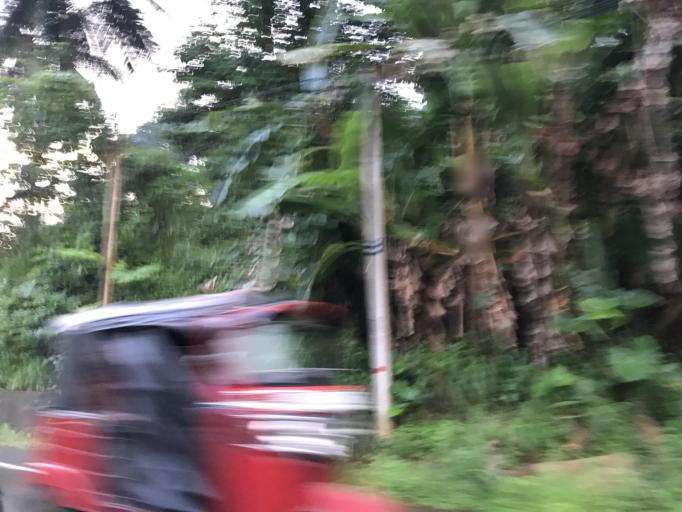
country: LK
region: Western
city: Horawala Junction
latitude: 6.5220
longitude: 80.2046
